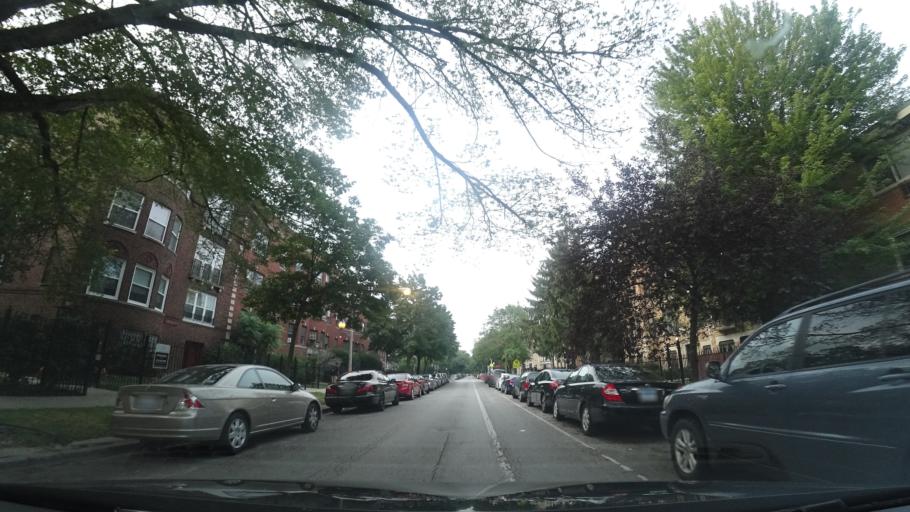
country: US
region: Illinois
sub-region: Cook County
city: Evanston
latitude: 41.9908
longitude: -87.6583
